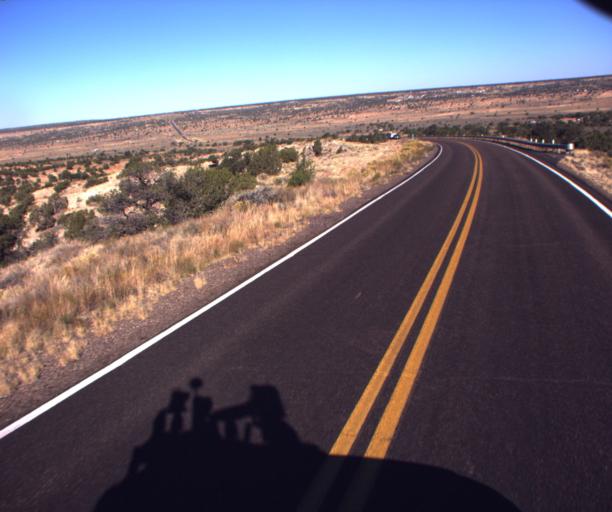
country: US
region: Arizona
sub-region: Navajo County
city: First Mesa
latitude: 35.7428
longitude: -110.1199
